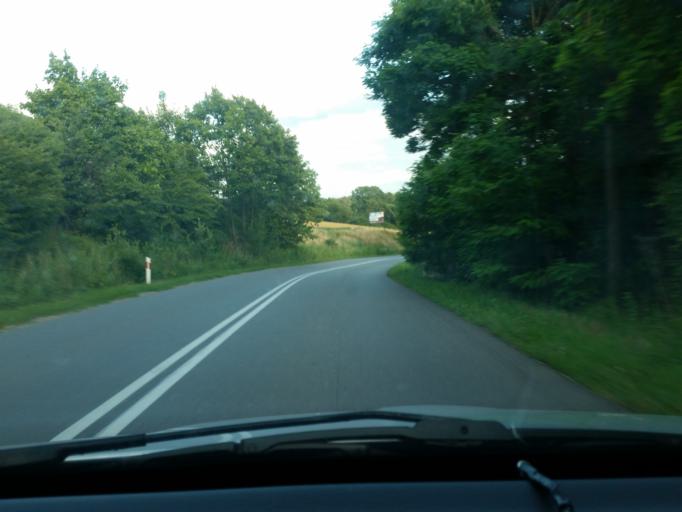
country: PL
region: Pomeranian Voivodeship
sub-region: Powiat czluchowski
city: Przechlewo
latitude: 53.8185
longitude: 17.4079
